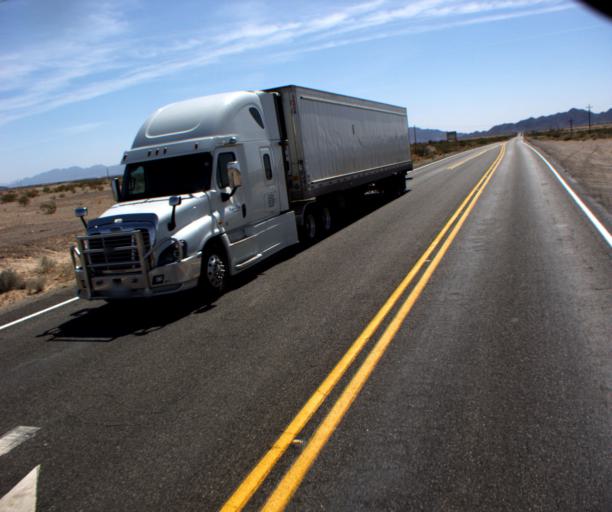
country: US
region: Arizona
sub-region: Yuma County
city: Fortuna Foothills
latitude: 32.8579
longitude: -114.3604
